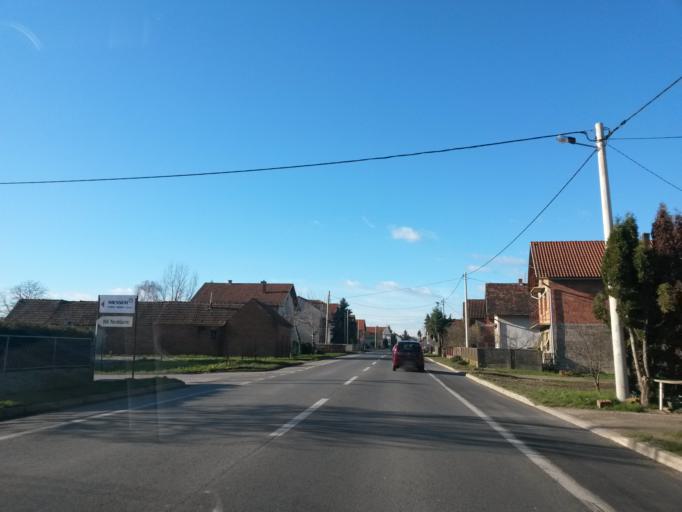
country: HR
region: Varazdinska
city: Nedeljanec
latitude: 46.2883
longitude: 16.2846
